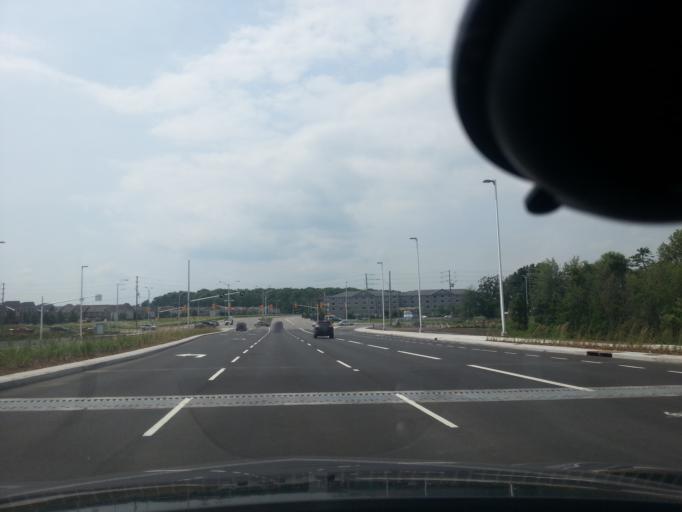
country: CA
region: Ontario
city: Bells Corners
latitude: 45.2702
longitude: -75.7030
